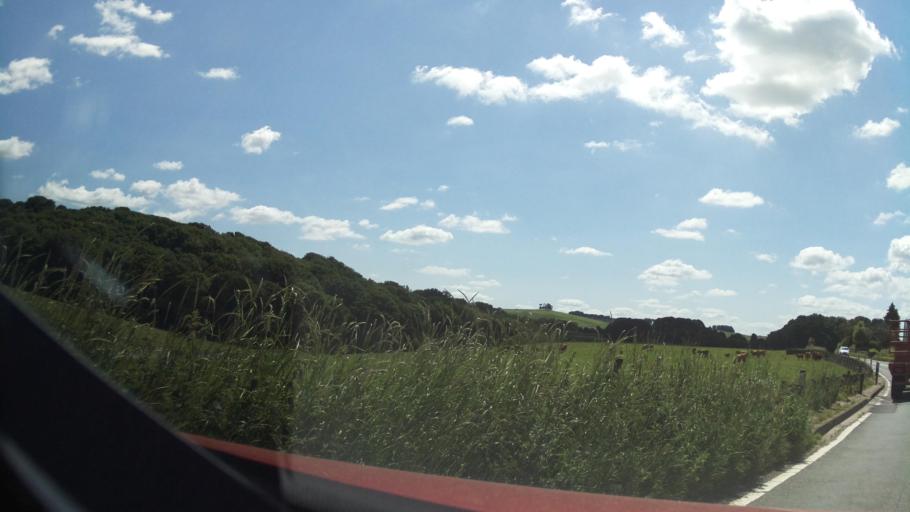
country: GB
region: England
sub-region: Derbyshire
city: Ashbourne
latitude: 53.1009
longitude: -1.7709
